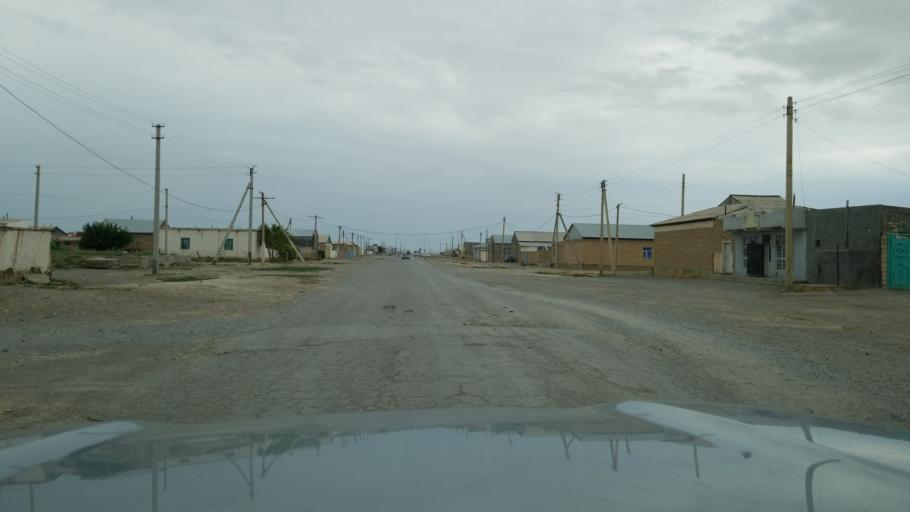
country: TM
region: Balkan
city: Serdar
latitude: 38.9922
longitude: 56.2780
